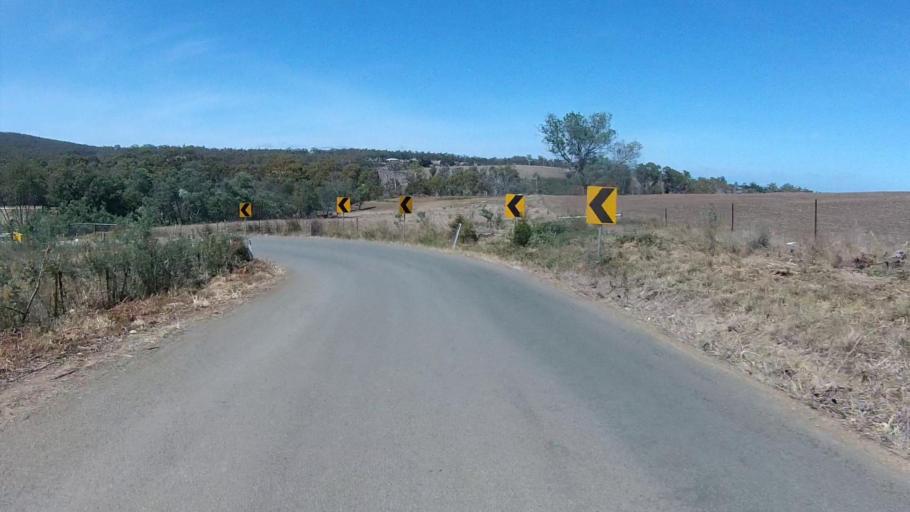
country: AU
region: Tasmania
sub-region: Sorell
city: Sorell
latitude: -42.7980
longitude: 147.6403
